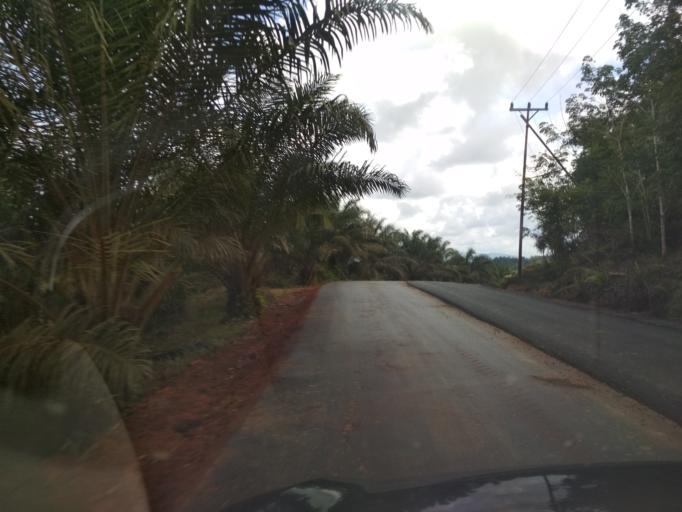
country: ID
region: West Kalimantan
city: Tayan
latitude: 0.5338
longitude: 110.0860
